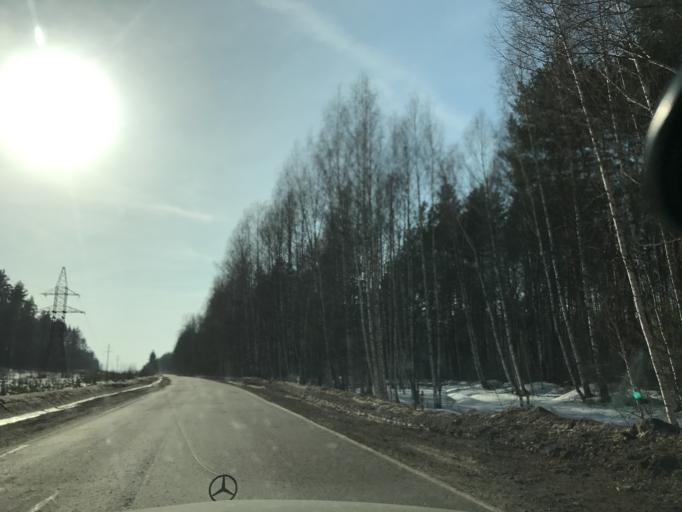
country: RU
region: Nizjnij Novgorod
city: Taremskoye
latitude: 56.0083
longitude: 42.9223
